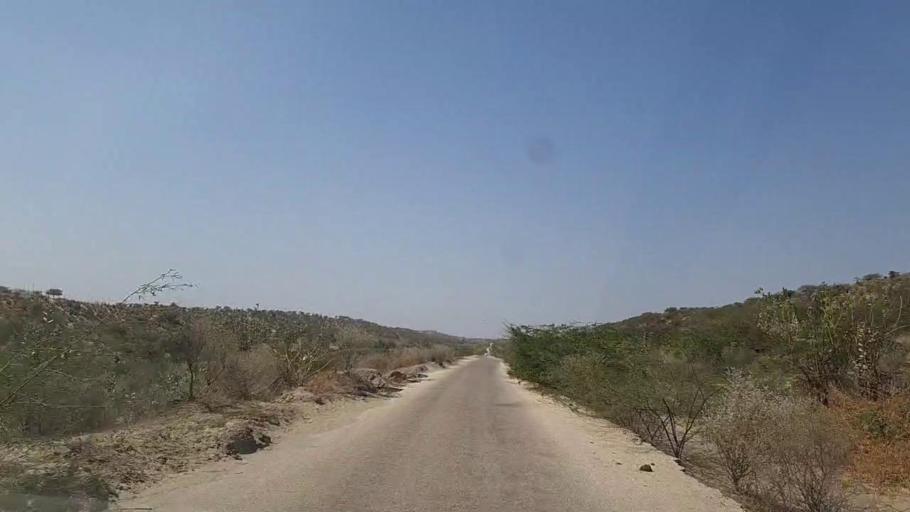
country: PK
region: Sindh
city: Diplo
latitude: 24.5177
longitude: 69.3461
